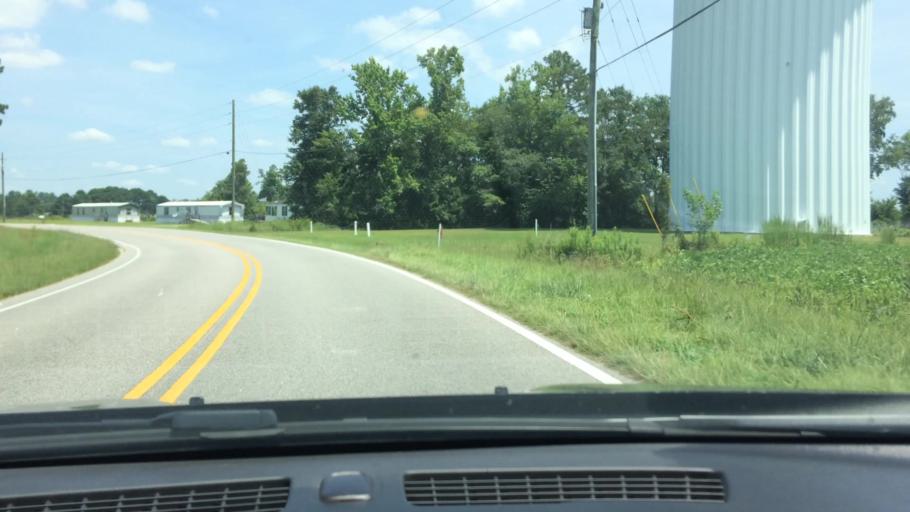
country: US
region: North Carolina
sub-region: Pitt County
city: Windsor
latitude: 35.5330
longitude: -77.3023
